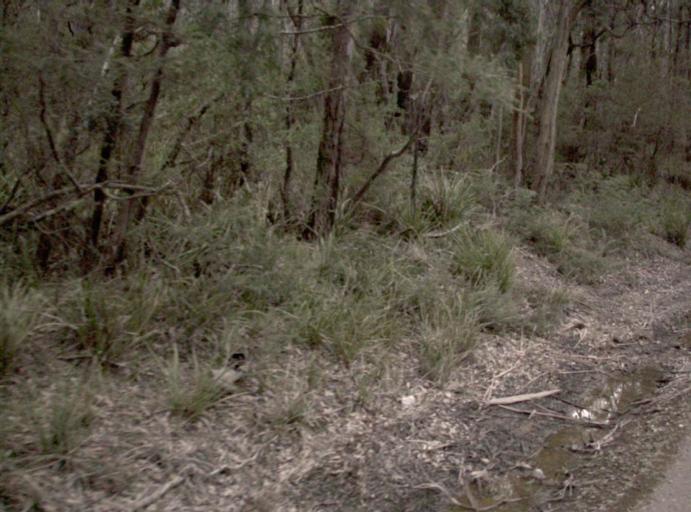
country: AU
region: Tasmania
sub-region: Launceston
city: Mayfield
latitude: -41.3529
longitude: 147.2212
